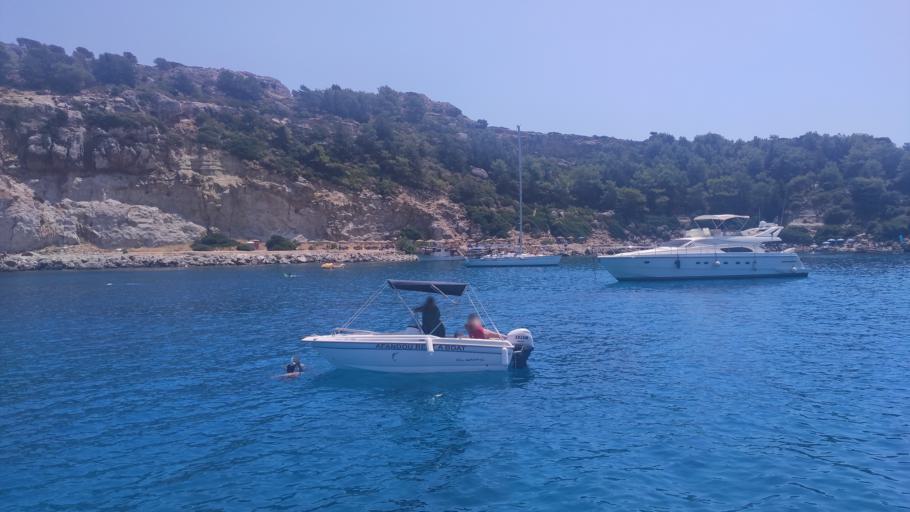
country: GR
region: South Aegean
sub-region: Nomos Dodekanisou
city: Faliraki
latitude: 36.3230
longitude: 28.2102
